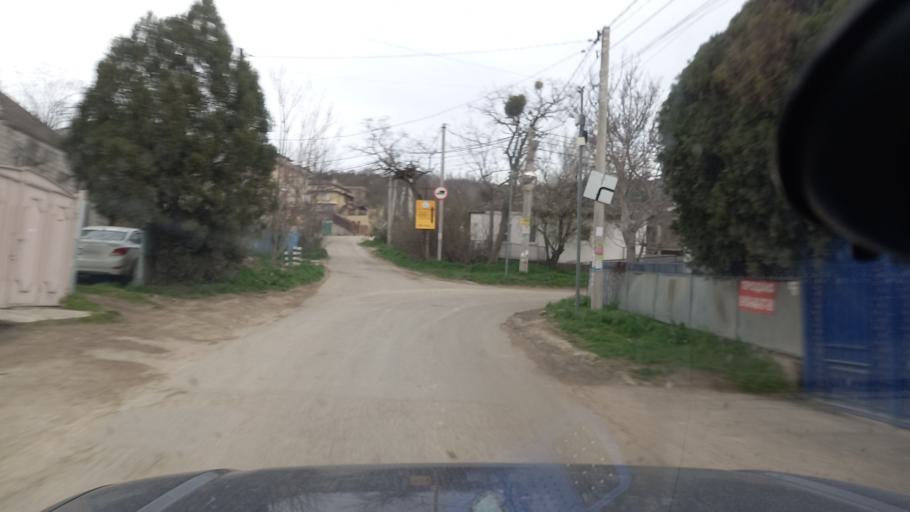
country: RU
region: Krasnodarskiy
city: Anapskaya
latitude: 44.8506
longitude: 37.3635
